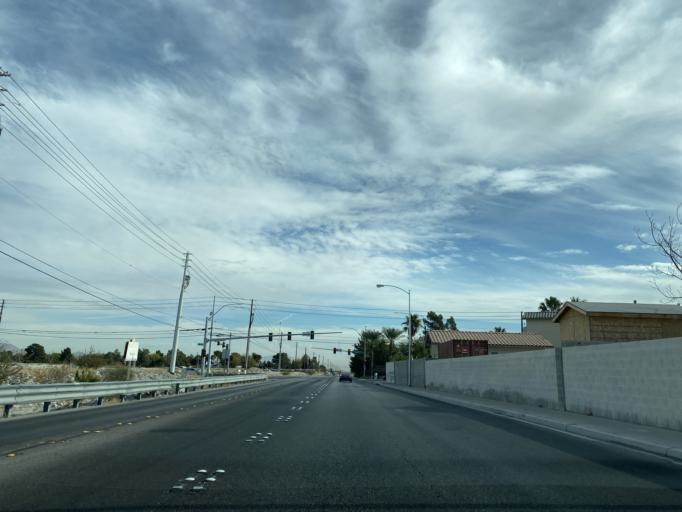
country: US
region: Nevada
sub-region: Clark County
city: North Las Vegas
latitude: 36.2468
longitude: -115.1906
